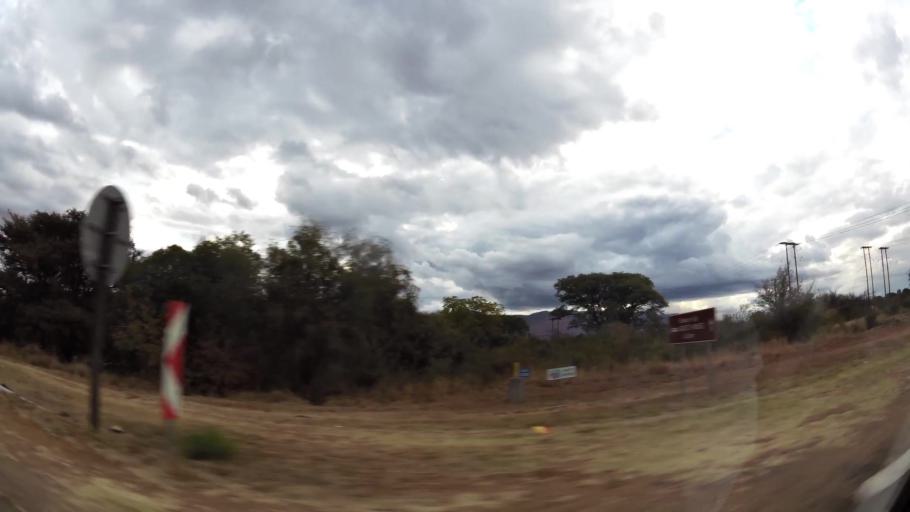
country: ZA
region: Limpopo
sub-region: Waterberg District Municipality
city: Mokopane
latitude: -24.2155
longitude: 29.0056
